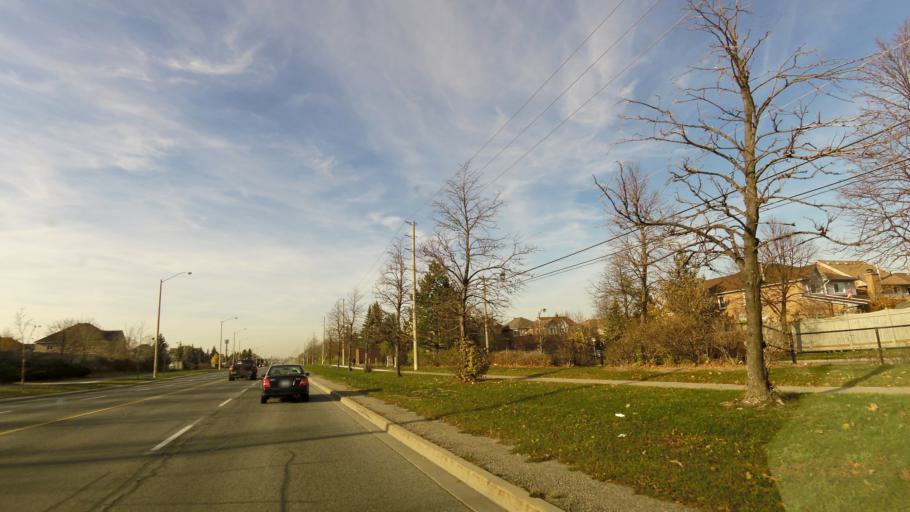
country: CA
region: Ontario
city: Brampton
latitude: 43.7595
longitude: -79.7407
